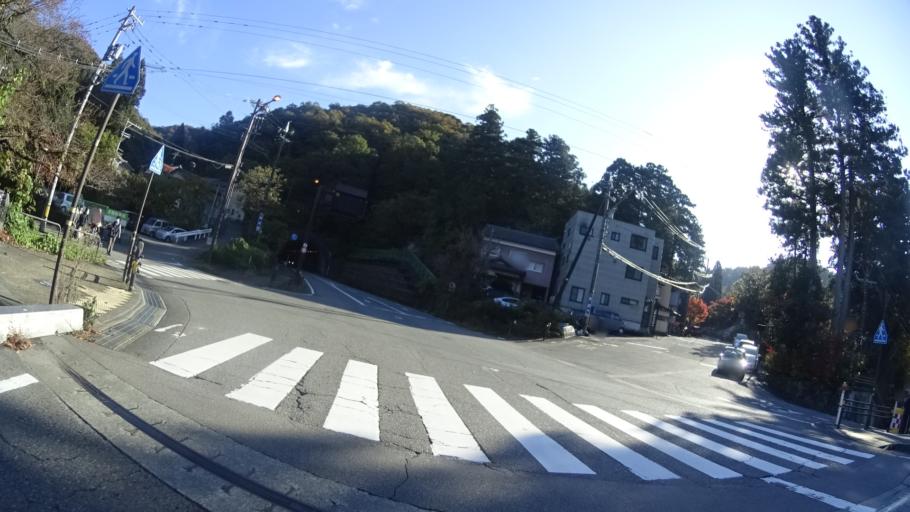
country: JP
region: Fukui
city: Maruoka
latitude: 36.2511
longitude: 136.3760
